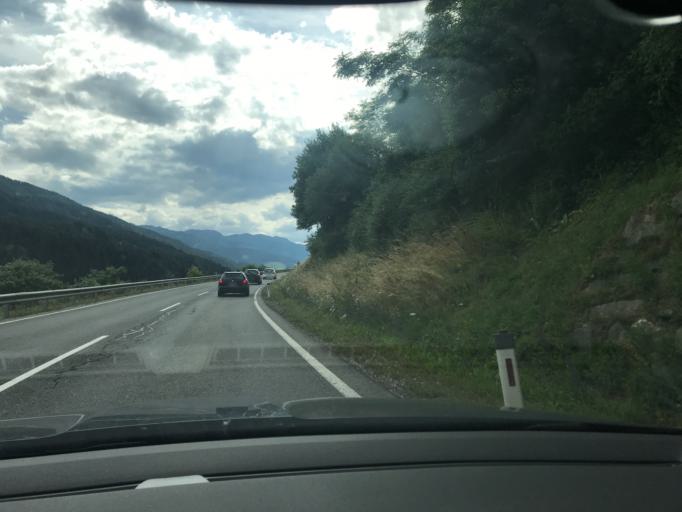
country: AT
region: Tyrol
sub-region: Politischer Bezirk Lienz
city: Abfaltersbach
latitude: 46.7586
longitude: 12.5362
